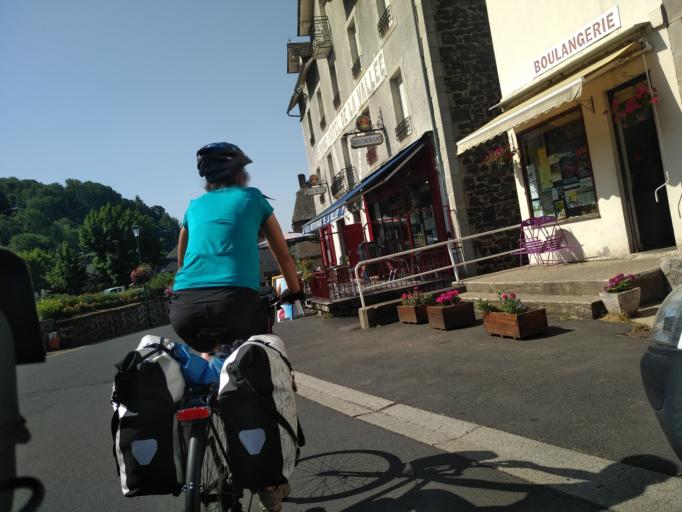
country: FR
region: Auvergne
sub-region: Departement du Cantal
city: Riom-es-Montagnes
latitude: 45.2099
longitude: 2.7167
